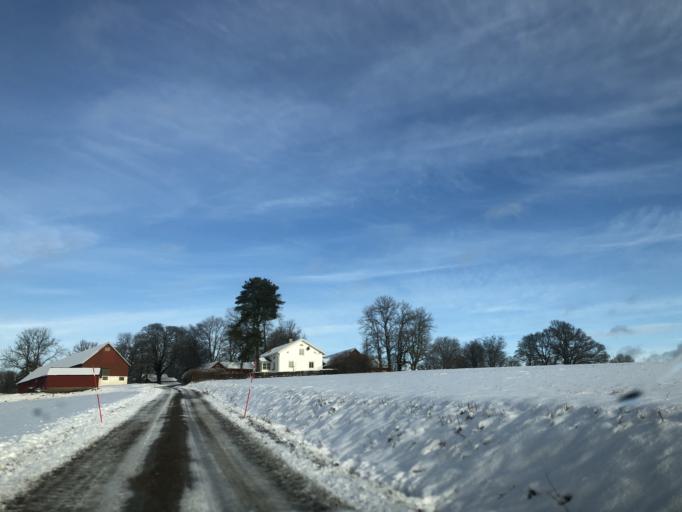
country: SE
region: Vaestra Goetaland
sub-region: Ulricehamns Kommun
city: Ulricehamn
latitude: 57.7293
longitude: 13.4755
